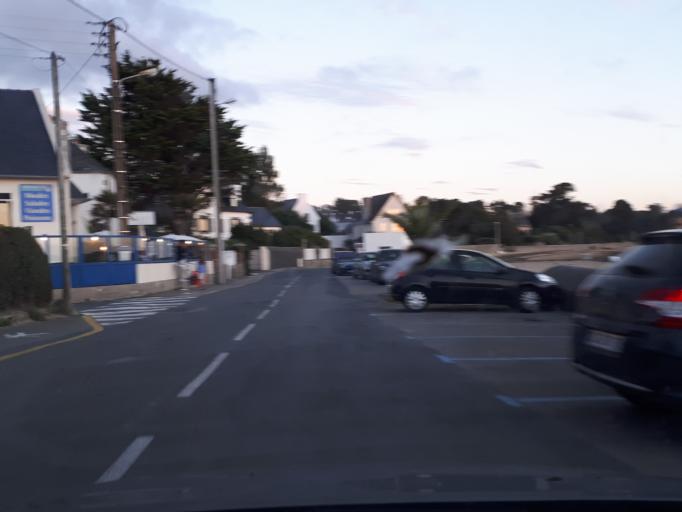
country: FR
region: Brittany
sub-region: Departement du Finistere
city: Carantec
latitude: 48.6728
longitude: -3.9227
